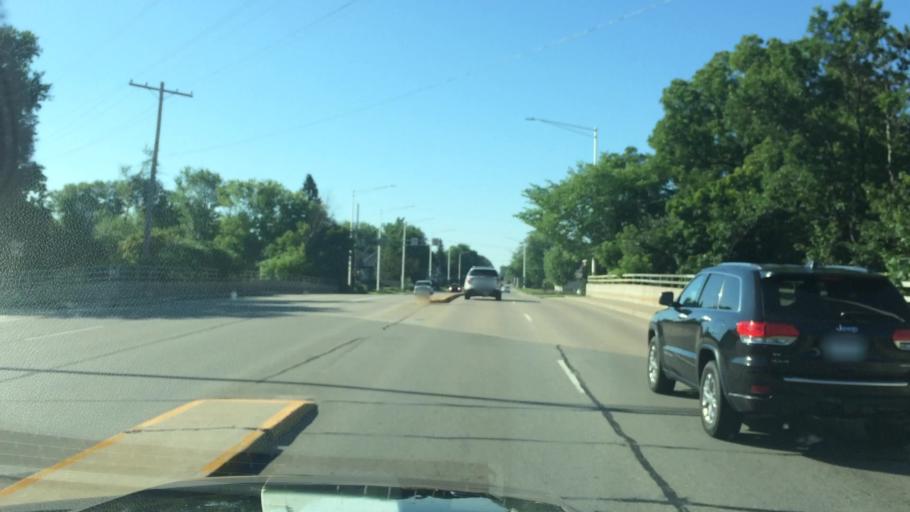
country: US
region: Wisconsin
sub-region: Marathon County
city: Wausau
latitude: 44.9500
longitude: -89.6222
